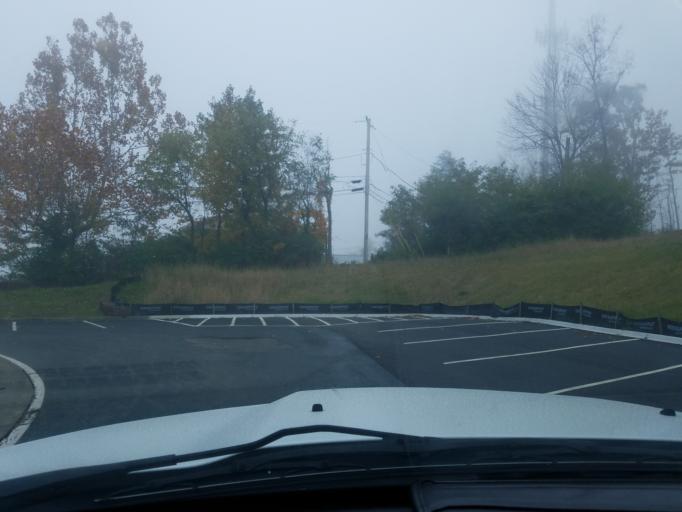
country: US
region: Indiana
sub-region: Floyd County
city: New Albany
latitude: 38.3083
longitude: -85.8445
